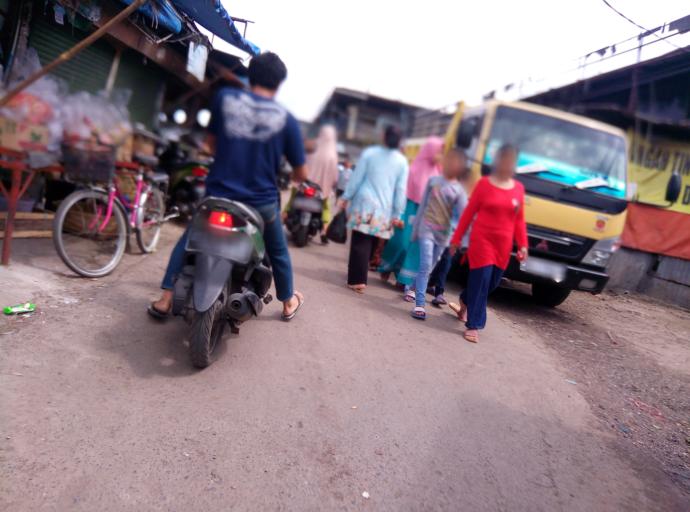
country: ID
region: West Java
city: Bandung
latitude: -6.9265
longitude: 107.6456
